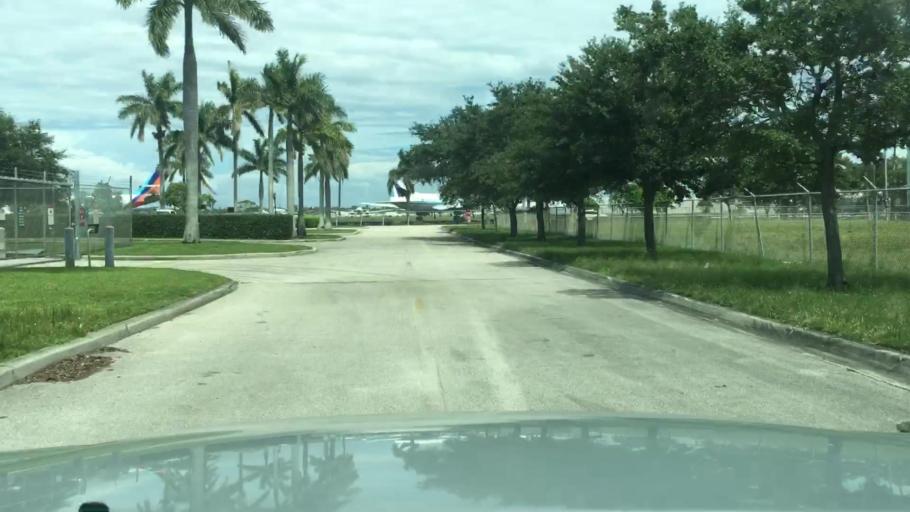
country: US
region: Florida
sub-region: Miami-Dade County
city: Opa-locka
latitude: 25.9079
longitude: -80.2691
